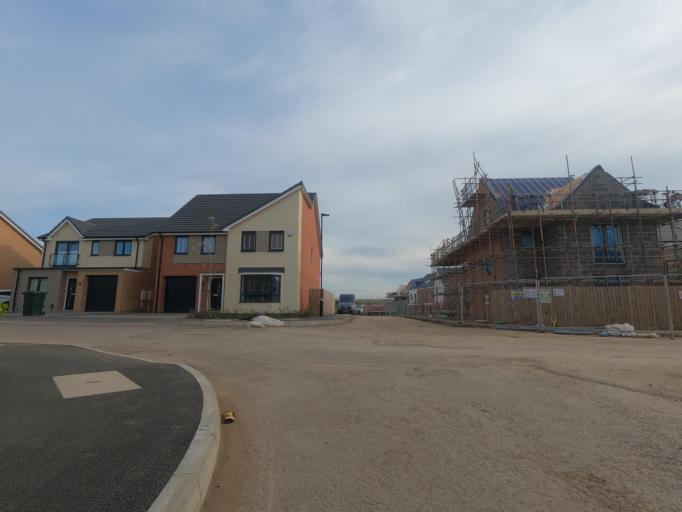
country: GB
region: England
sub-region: Newcastle upon Tyne
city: Hazlerigg
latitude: 55.0269
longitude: -1.6599
